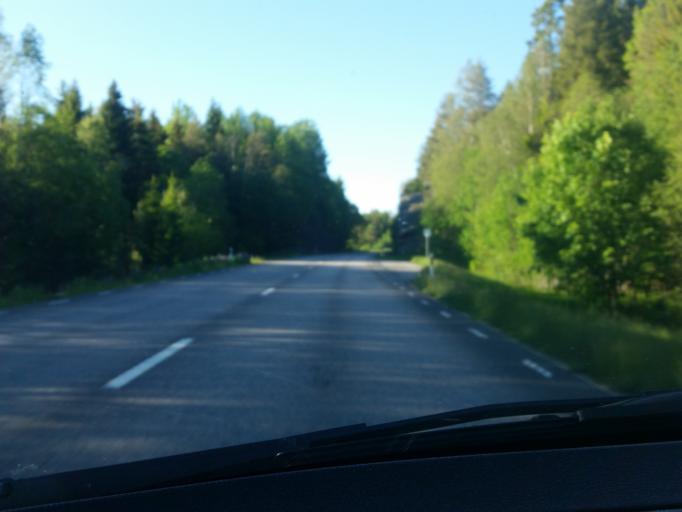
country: SE
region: Vaestra Goetaland
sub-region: Fargelanda Kommun
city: Faergelanda
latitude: 58.5283
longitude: 11.9792
